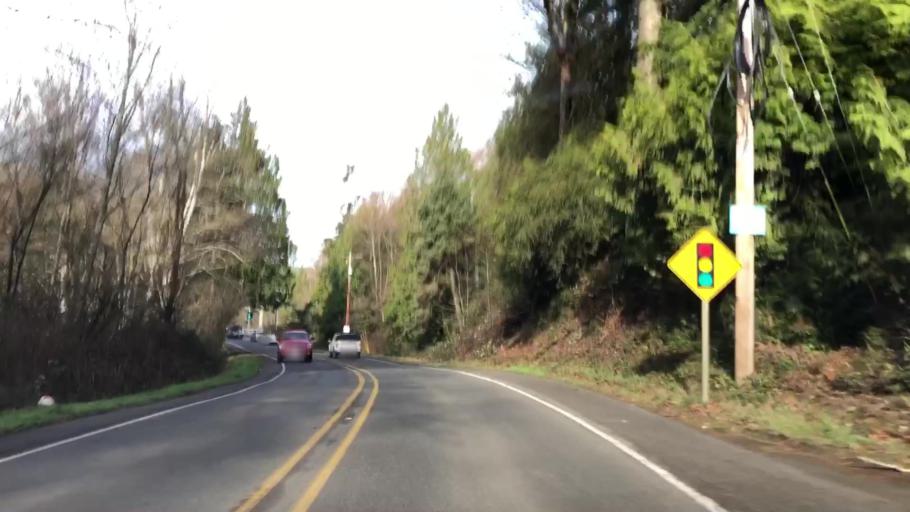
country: US
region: Washington
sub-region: Kitsap County
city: Indianola
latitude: 47.7731
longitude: -122.5552
